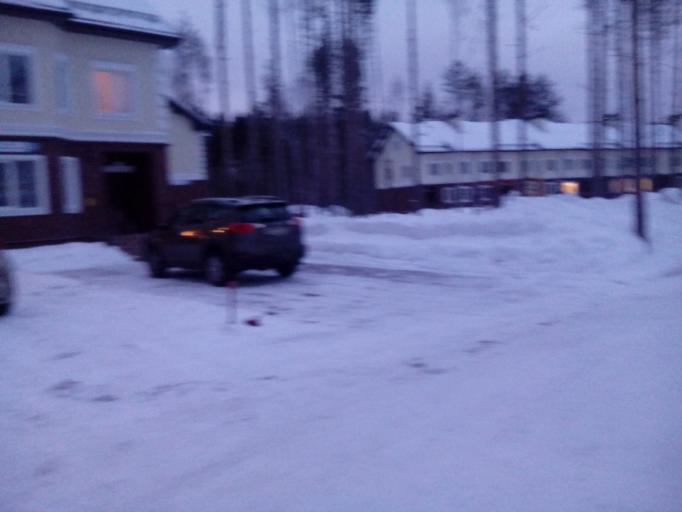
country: RU
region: Sverdlovsk
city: Shirokaya Rechka
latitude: 56.8075
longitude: 60.4762
